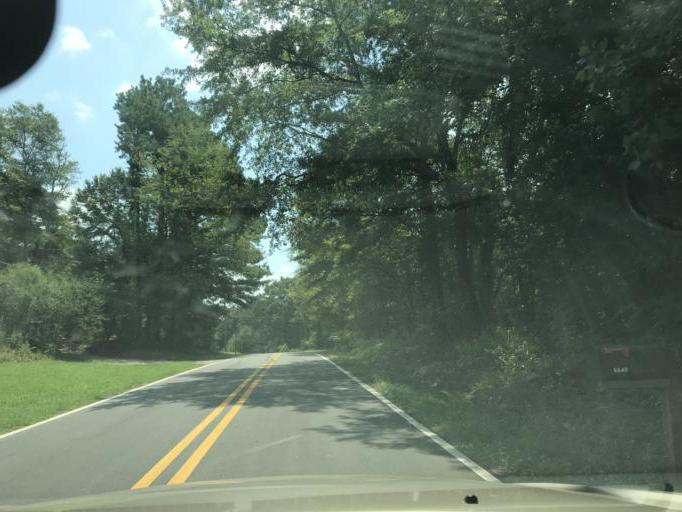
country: US
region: Georgia
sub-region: Forsyth County
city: Cumming
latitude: 34.3008
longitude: -84.1810
